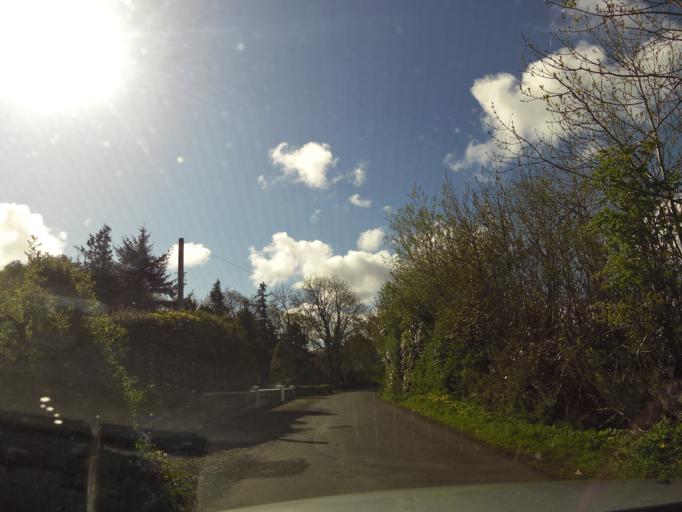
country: IE
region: Connaught
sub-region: Maigh Eo
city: Kiltamagh
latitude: 53.7850
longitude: -8.9616
